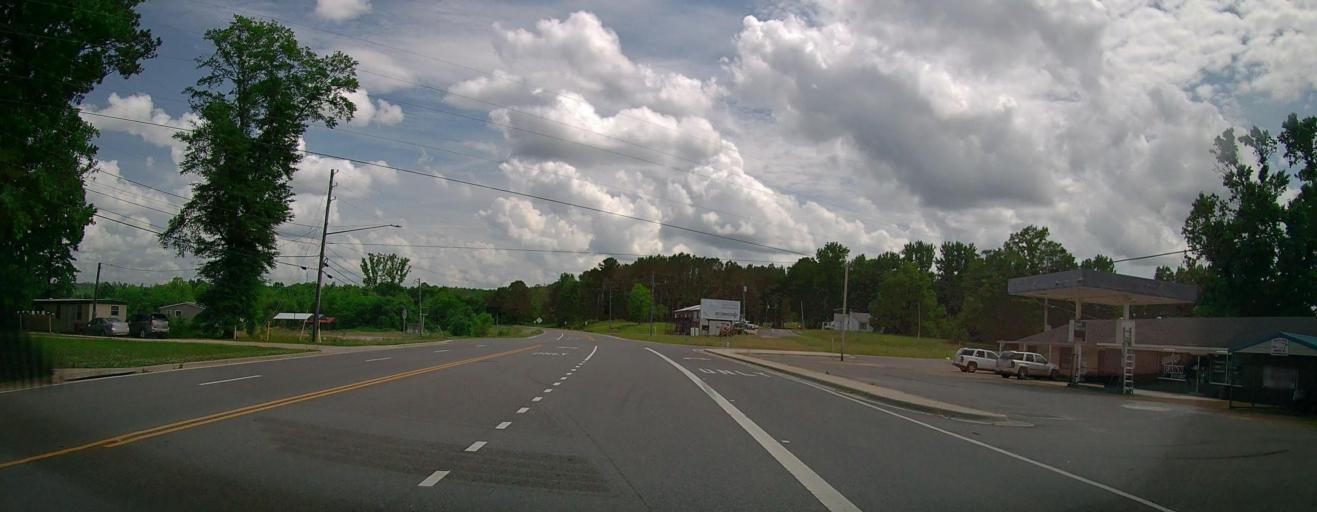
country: US
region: Alabama
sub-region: Marion County
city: Hamilton
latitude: 34.1004
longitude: -87.9889
